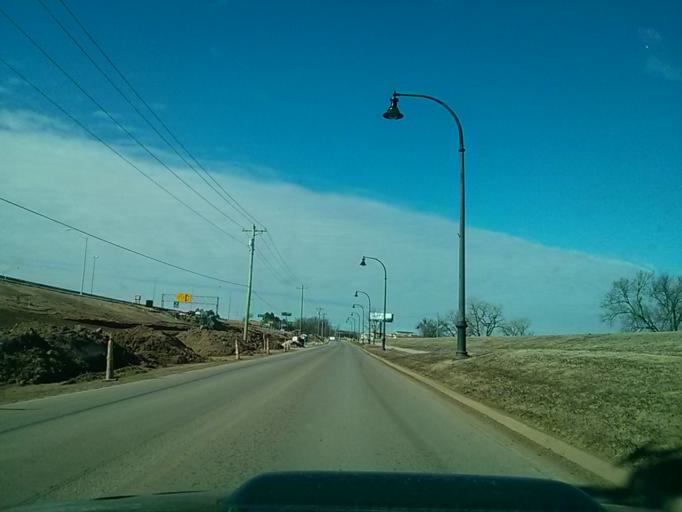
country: US
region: Oklahoma
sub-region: Tulsa County
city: Jenks
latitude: 36.0173
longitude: -95.9694
